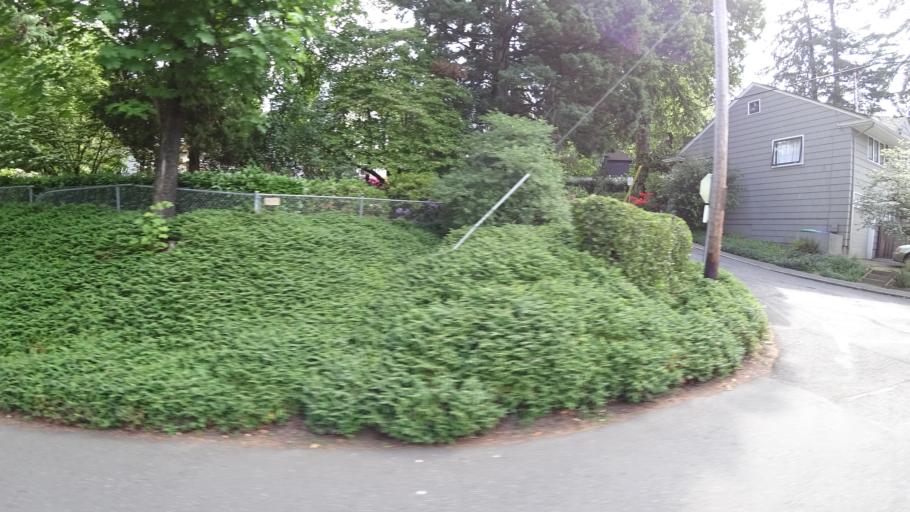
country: US
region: Oregon
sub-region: Multnomah County
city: Portland
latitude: 45.5070
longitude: -122.7047
